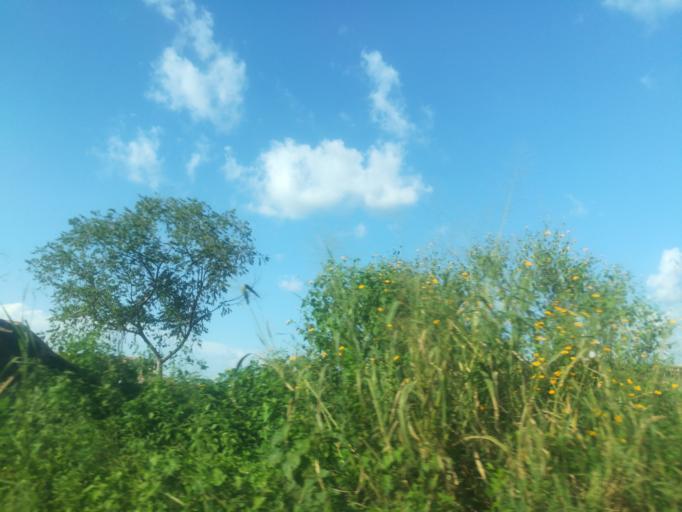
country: NG
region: Oyo
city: Ibadan
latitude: 7.4359
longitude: 3.9715
